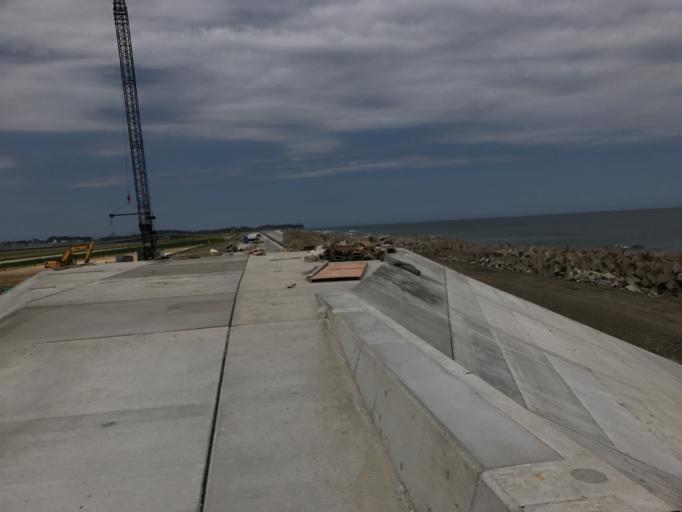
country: JP
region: Miyagi
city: Marumori
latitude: 37.7952
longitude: 140.9861
